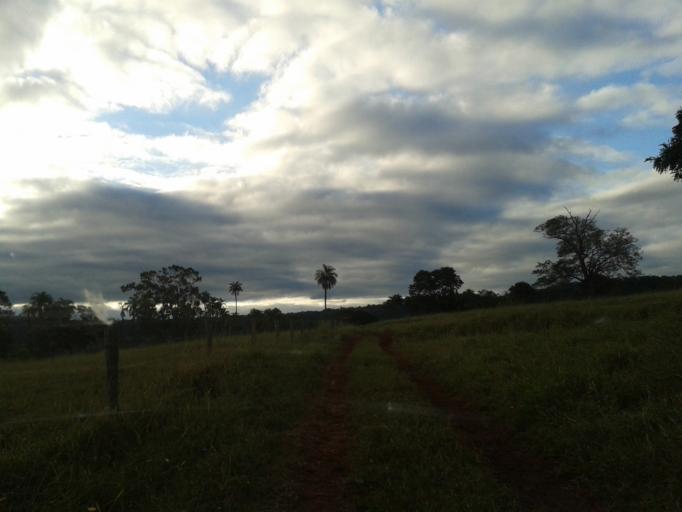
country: BR
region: Minas Gerais
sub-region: Campina Verde
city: Campina Verde
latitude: -19.4653
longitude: -49.6522
